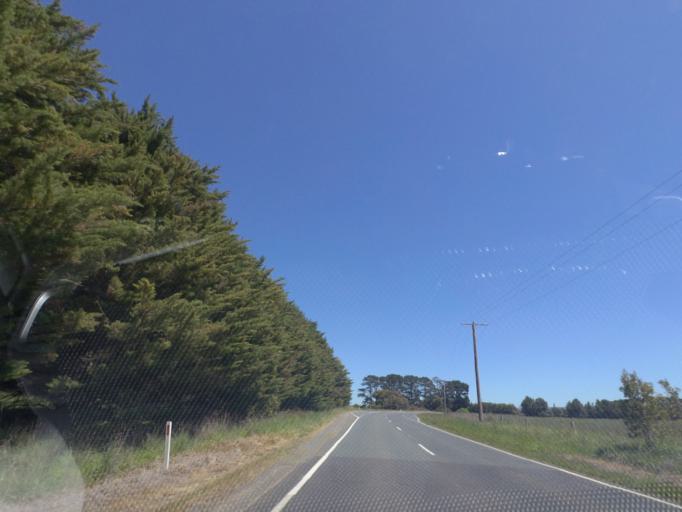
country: AU
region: Victoria
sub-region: Hume
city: Sunbury
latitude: -37.2848
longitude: 144.7579
